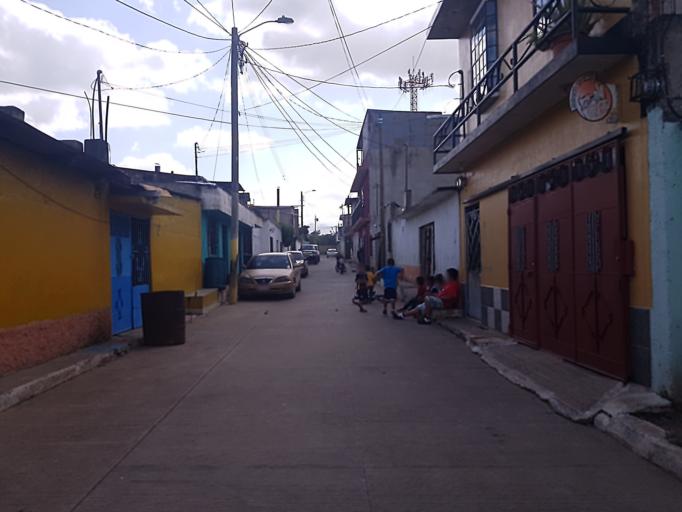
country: GT
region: Guatemala
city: Petapa
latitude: 14.5030
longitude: -90.5554
